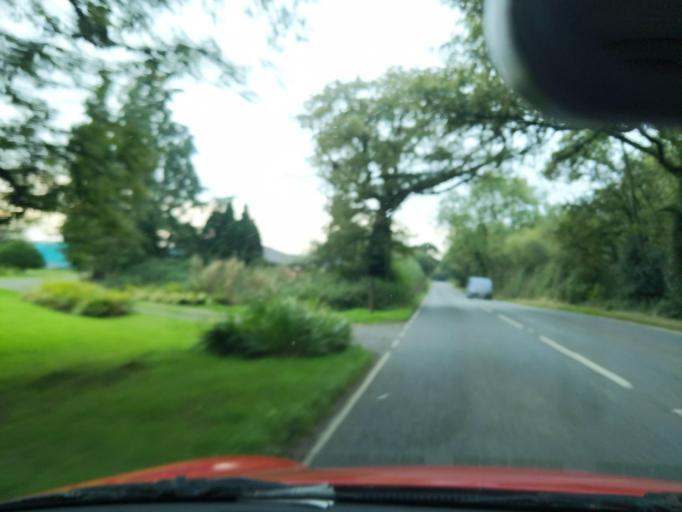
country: GB
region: England
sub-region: Devon
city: Okehampton
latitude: 50.7949
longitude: -4.0395
